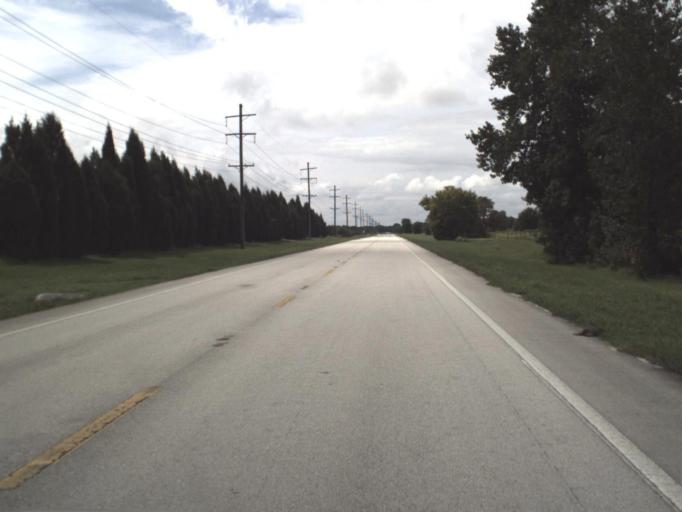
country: US
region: Florida
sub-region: Hardee County
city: Bowling Green
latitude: 27.5936
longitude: -82.0679
